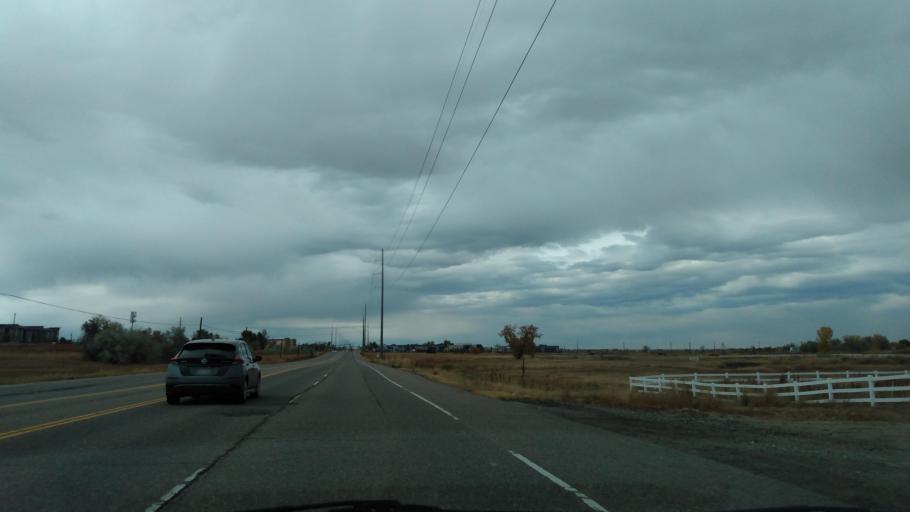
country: US
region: Colorado
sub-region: Adams County
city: Northglenn
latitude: 39.9504
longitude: -104.9782
